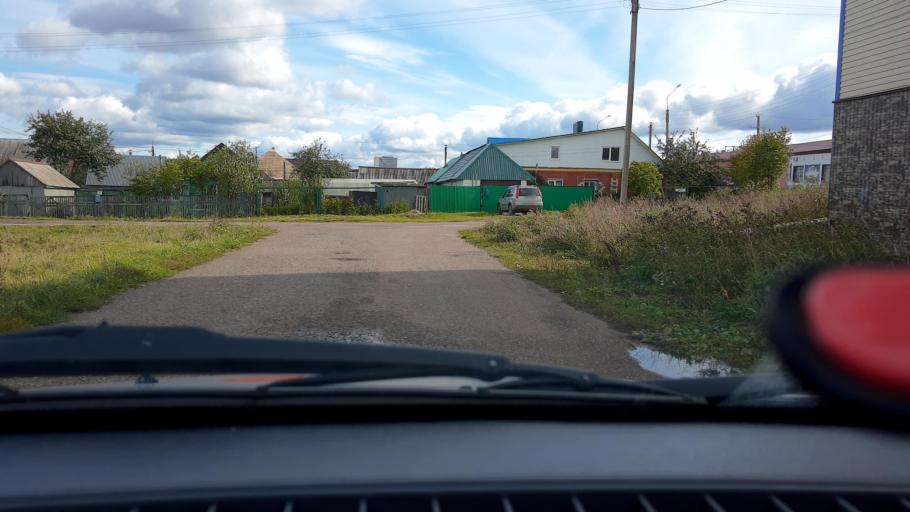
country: RU
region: Bashkortostan
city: Belebey
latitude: 54.0971
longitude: 54.1251
